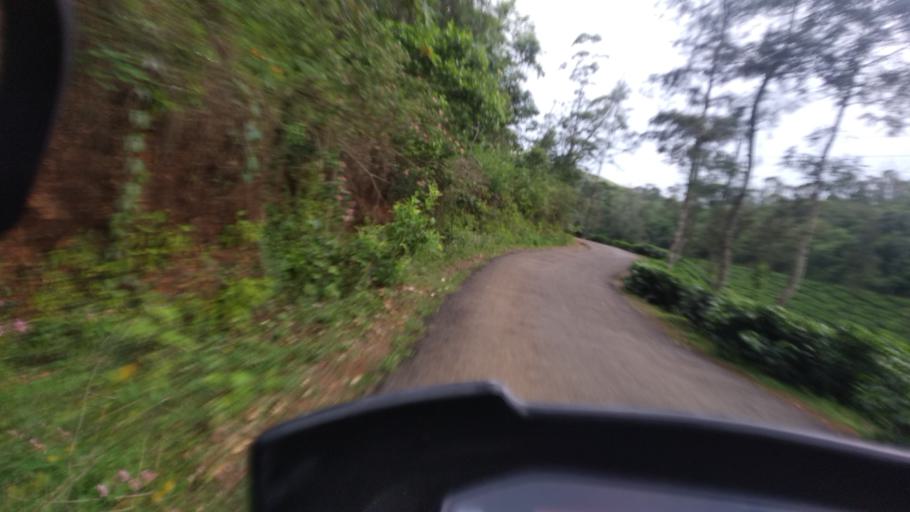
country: IN
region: Tamil Nadu
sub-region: Theni
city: Gudalur
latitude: 9.5453
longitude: 77.0512
